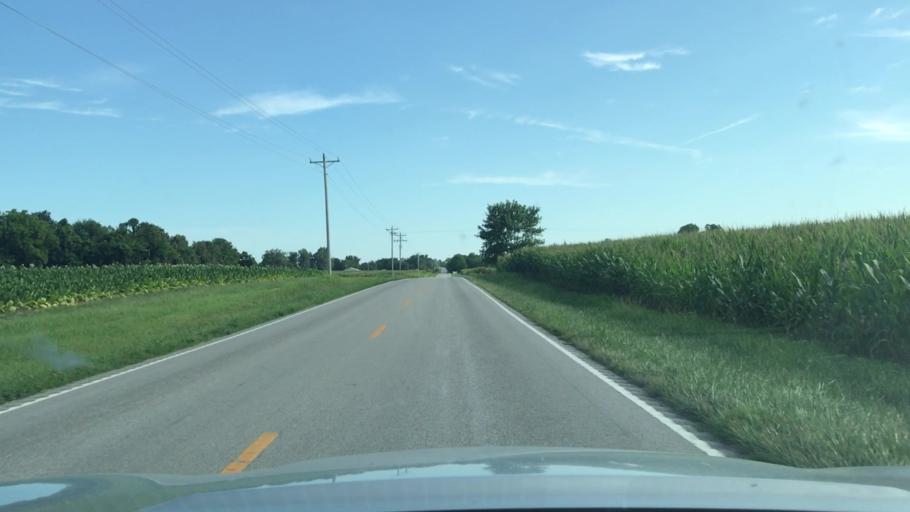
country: US
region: Kentucky
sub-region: Todd County
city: Elkton
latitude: 36.9180
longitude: -87.1629
